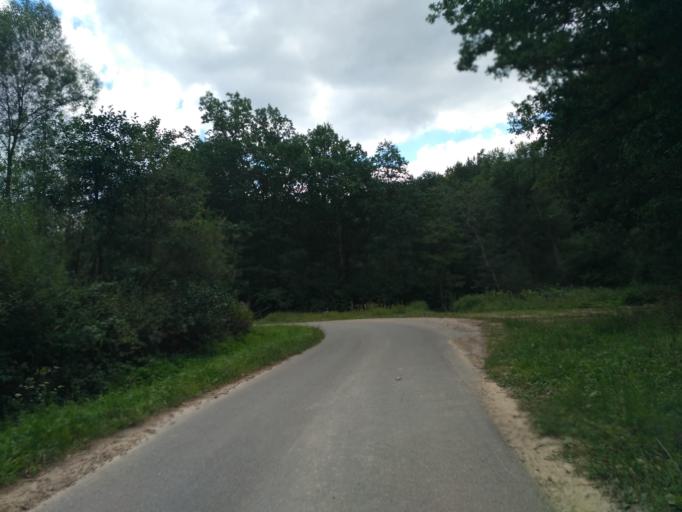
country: PL
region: Subcarpathian Voivodeship
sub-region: Powiat rzeszowski
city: Dynow
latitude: 49.7583
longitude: 22.2854
